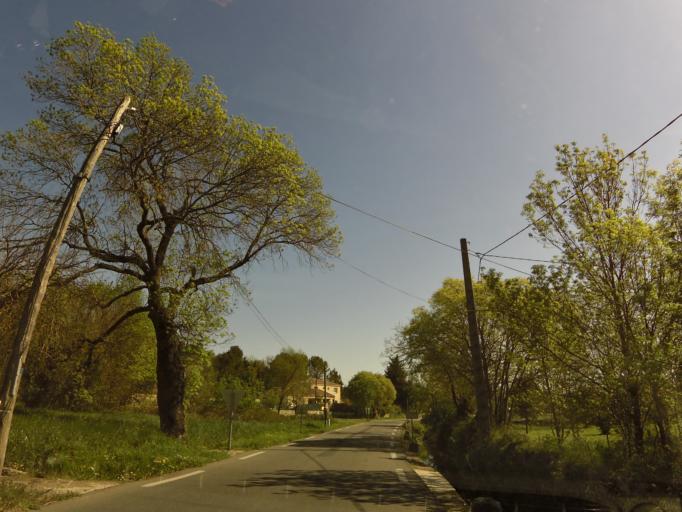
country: FR
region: Languedoc-Roussillon
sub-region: Departement du Gard
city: Aubais
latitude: 43.7490
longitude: 4.1396
